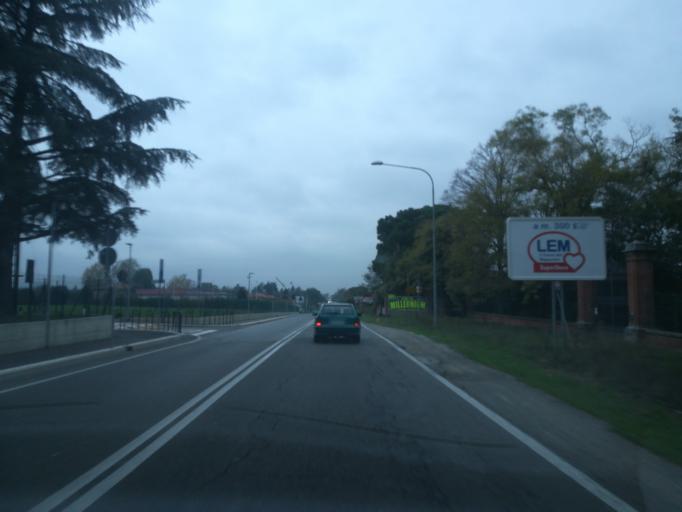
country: IT
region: Emilia-Romagna
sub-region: Provincia di Bologna
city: Toscanella
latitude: 44.3777
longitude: 11.6518
